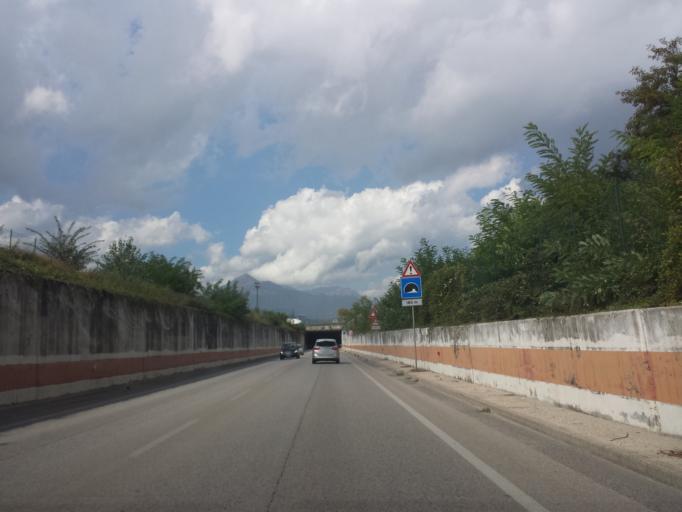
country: IT
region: Veneto
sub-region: Provincia di Vicenza
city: Cornedo Vicentino
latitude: 45.6066
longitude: 11.3474
